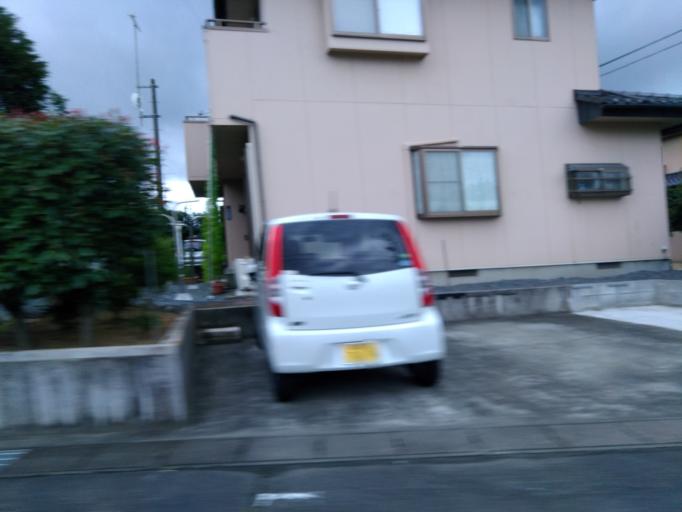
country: JP
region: Fukushima
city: Namie
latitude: 37.6329
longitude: 140.9283
